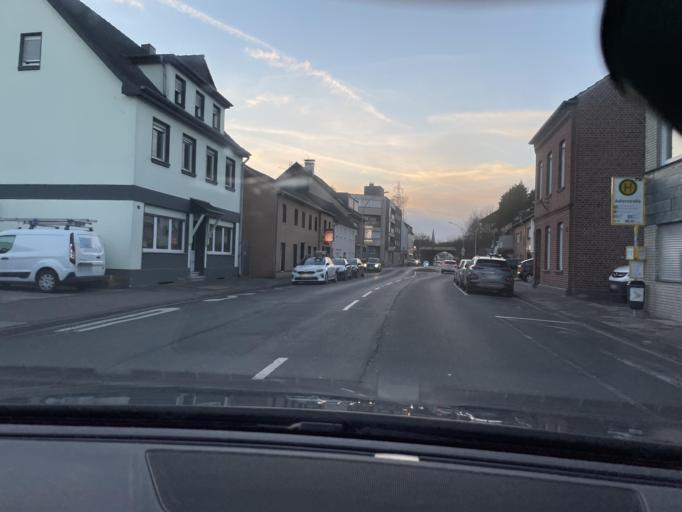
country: DE
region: North Rhine-Westphalia
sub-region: Regierungsbezirk Dusseldorf
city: Monchengladbach
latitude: 51.2240
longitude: 6.4640
